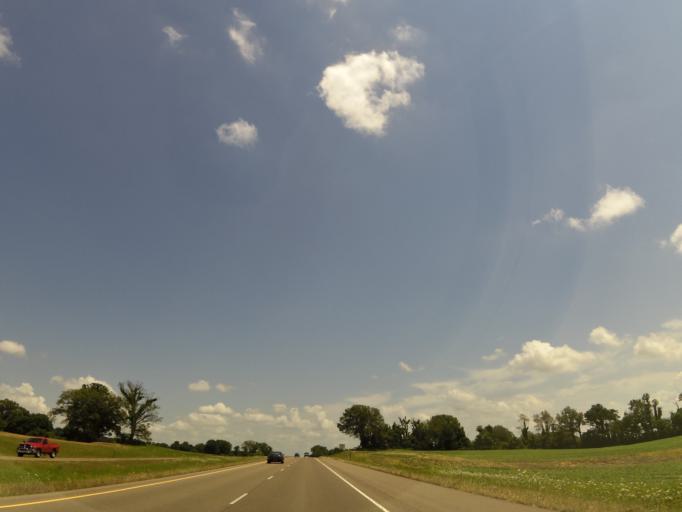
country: US
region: Tennessee
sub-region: Crockett County
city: Alamo
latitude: 35.8730
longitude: -89.2181
